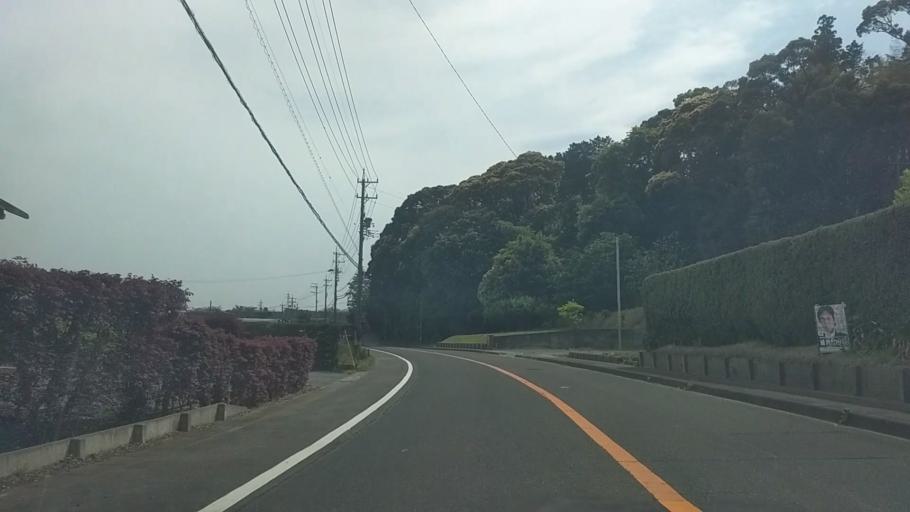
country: JP
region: Shizuoka
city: Kosai-shi
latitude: 34.7502
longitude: 137.6041
